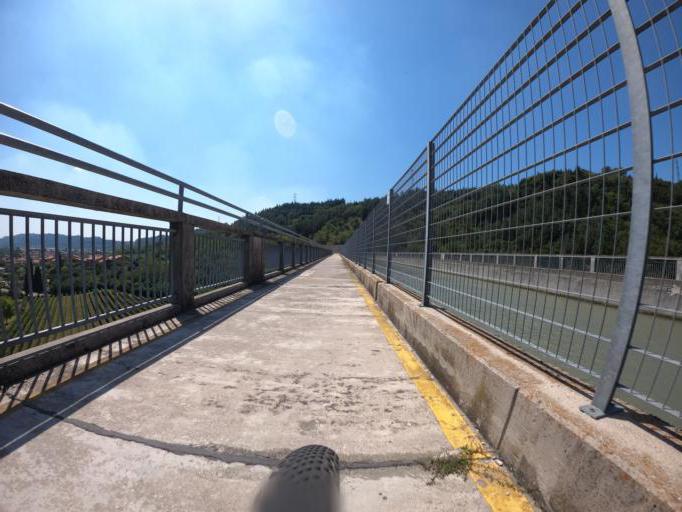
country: IT
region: Veneto
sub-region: Provincia di Verona
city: Volargne
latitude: 45.5281
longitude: 10.7992
